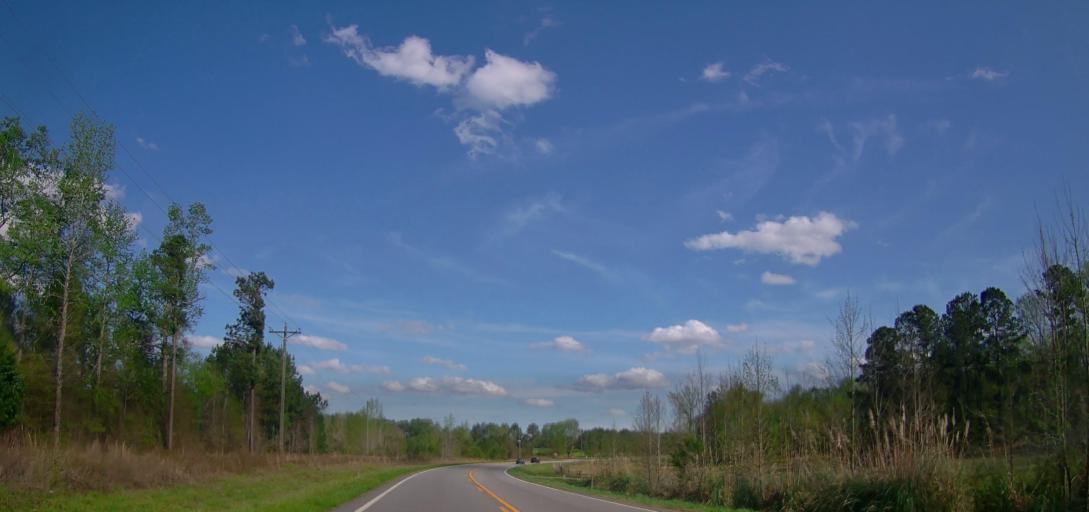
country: US
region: Georgia
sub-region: Baldwin County
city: Hardwick
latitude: 33.0786
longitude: -83.1428
